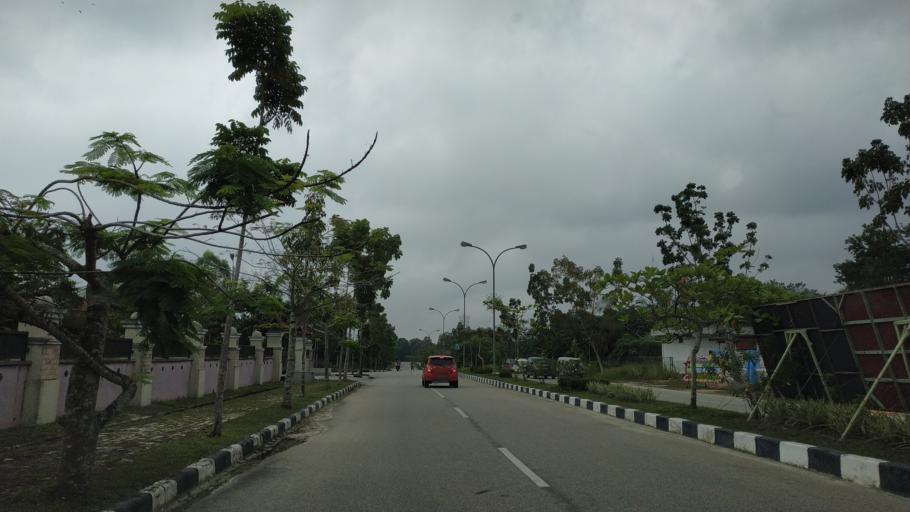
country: ID
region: Riau
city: Pangkalanbunut
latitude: 0.3842
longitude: 101.8242
